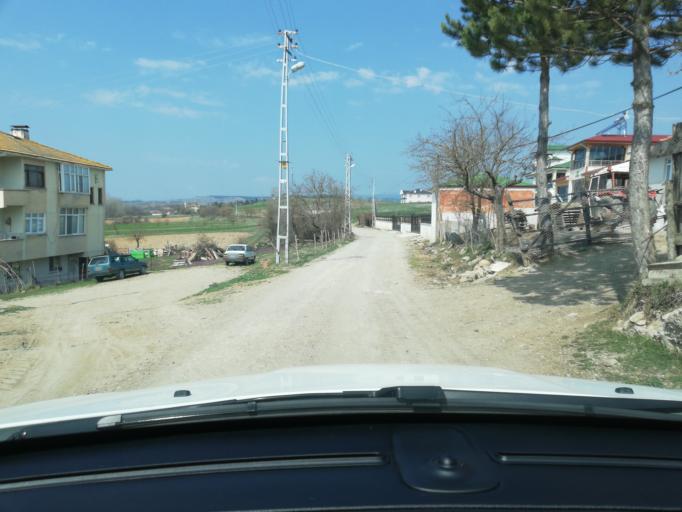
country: TR
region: Kastamonu
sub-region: Cide
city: Kastamonu
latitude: 41.4598
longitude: 33.7566
